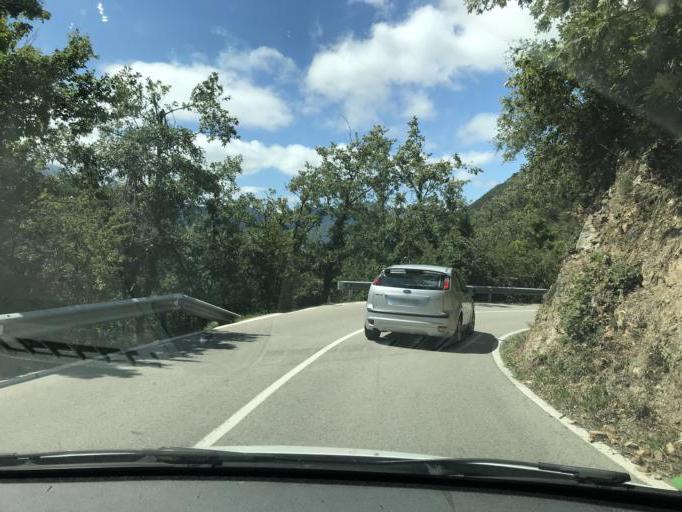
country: ES
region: Cantabria
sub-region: Provincia de Cantabria
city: Cabezon de Liebana
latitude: 43.0754
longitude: -4.5033
